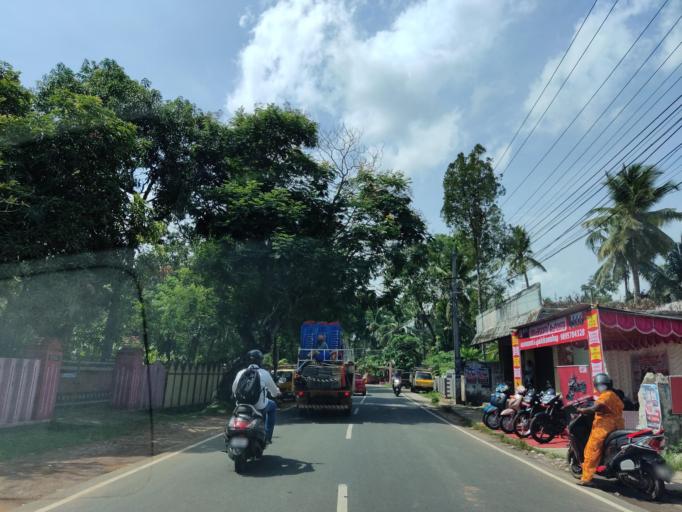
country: IN
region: Kerala
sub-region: Alappuzha
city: Mavelikara
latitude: 9.2667
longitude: 76.5407
